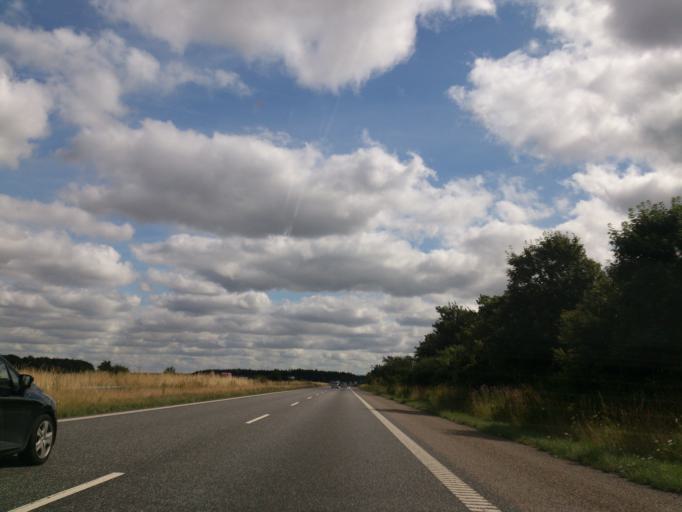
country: DK
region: South Denmark
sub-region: Aabenraa Kommune
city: Krusa
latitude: 54.8912
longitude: 9.3776
